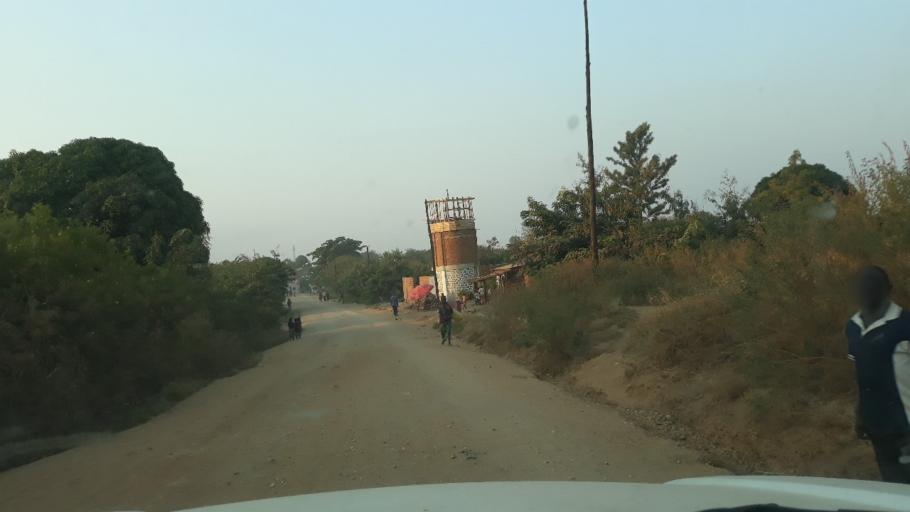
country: BI
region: Bururi
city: Rumonge
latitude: -4.1185
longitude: 29.0859
